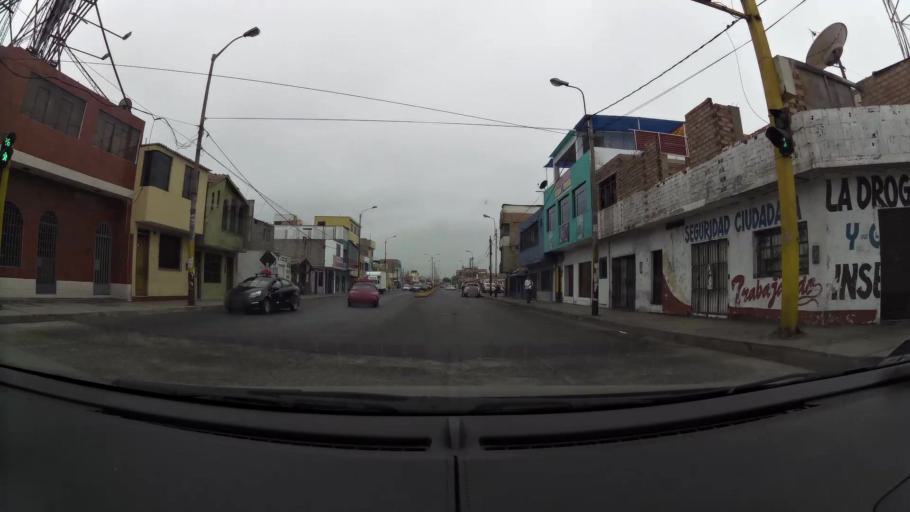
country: PE
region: Ancash
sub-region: Provincia de Santa
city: Chimbote
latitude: -9.0784
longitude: -78.5876
